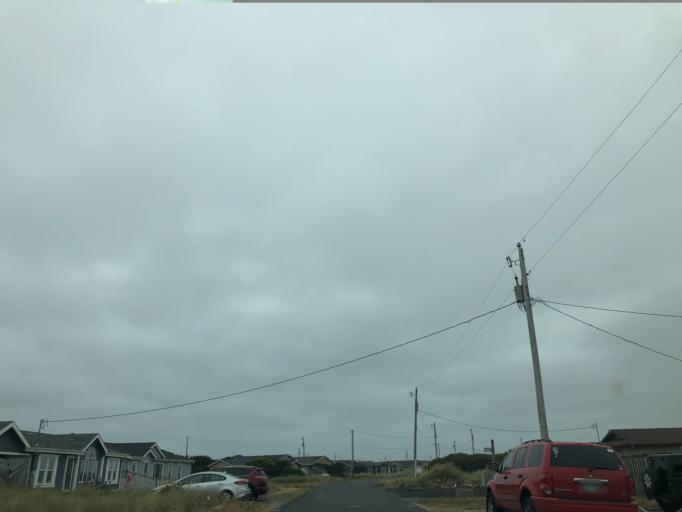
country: US
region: Oregon
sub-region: Lincoln County
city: Waldport
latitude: 44.4270
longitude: -124.0793
